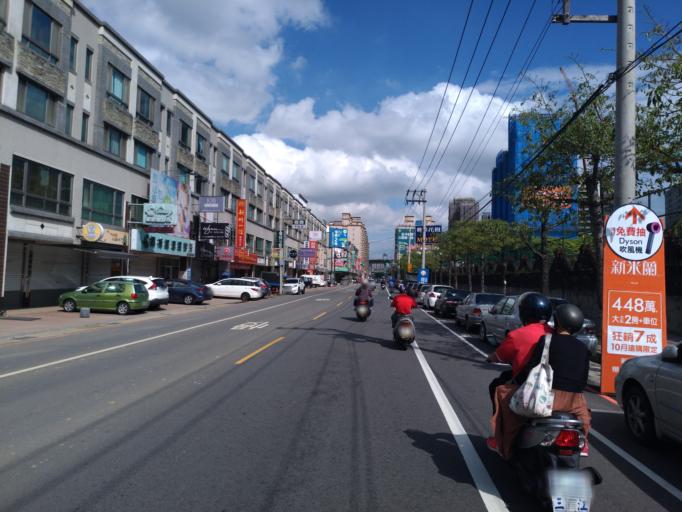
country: TW
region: Taiwan
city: Daxi
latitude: 24.9125
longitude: 121.1586
